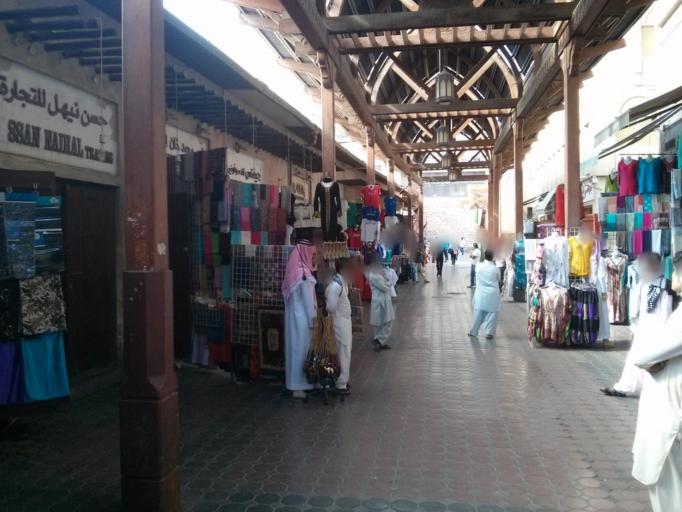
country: AE
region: Ash Shariqah
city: Sharjah
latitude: 25.2646
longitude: 55.2946
